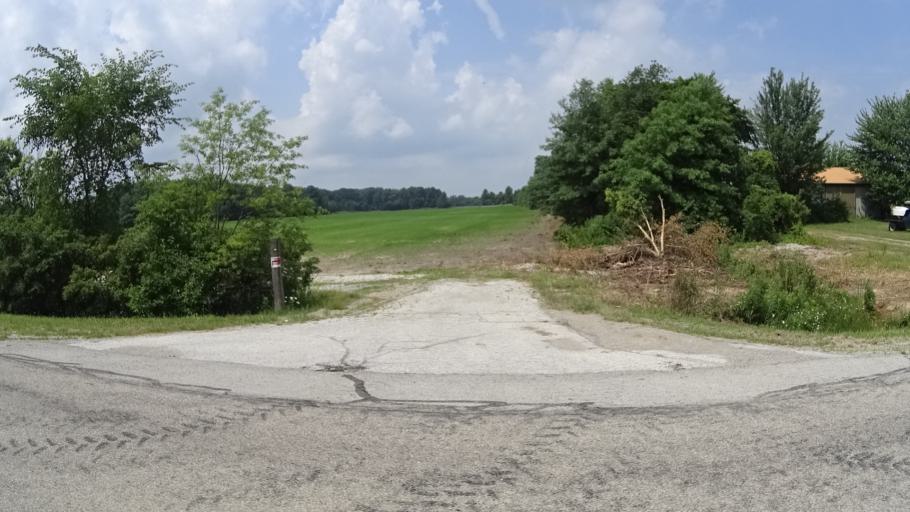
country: US
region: Ohio
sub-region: Lorain County
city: Vermilion
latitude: 41.3993
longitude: -82.3900
